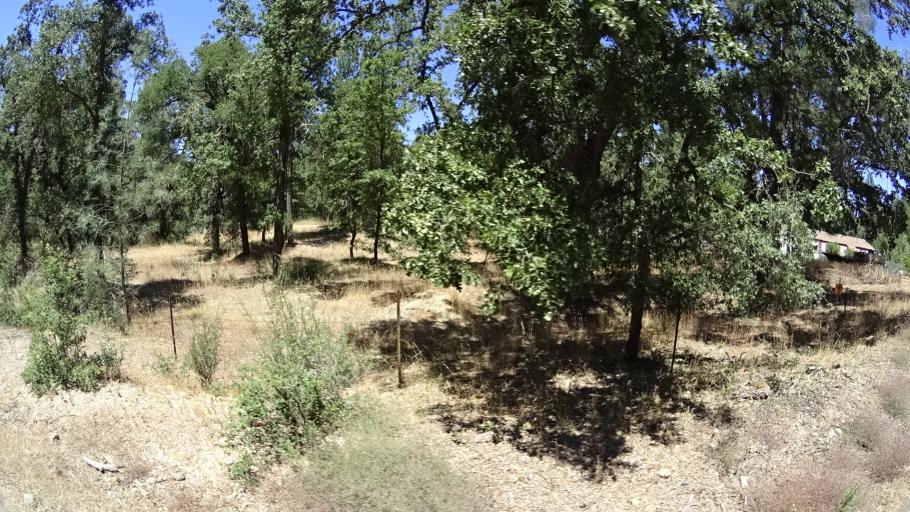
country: US
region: California
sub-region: Calaveras County
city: Mountain Ranch
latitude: 38.2640
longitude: -120.4905
